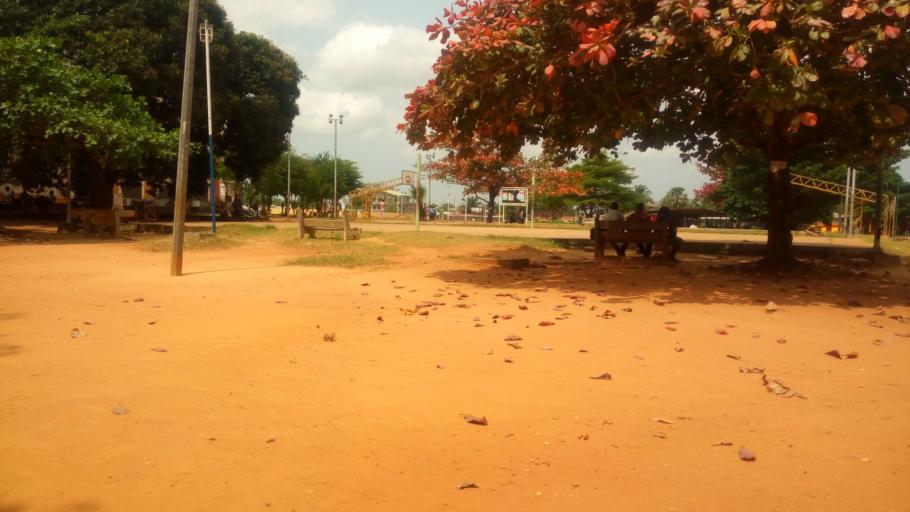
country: BJ
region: Atlantique
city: Abomey-Calavi
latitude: 6.4124
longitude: 2.3425
